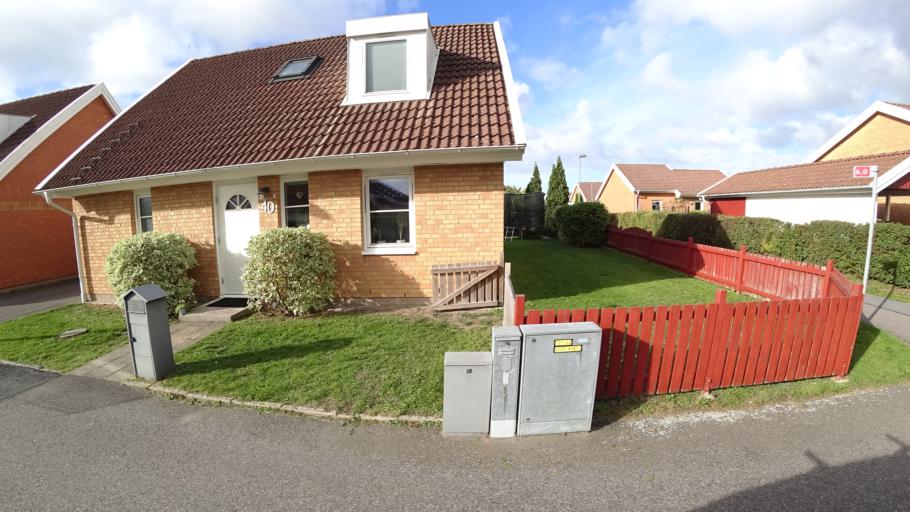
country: SE
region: Skane
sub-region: Kavlinge Kommun
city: Loddekopinge
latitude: 55.7616
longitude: 13.0261
